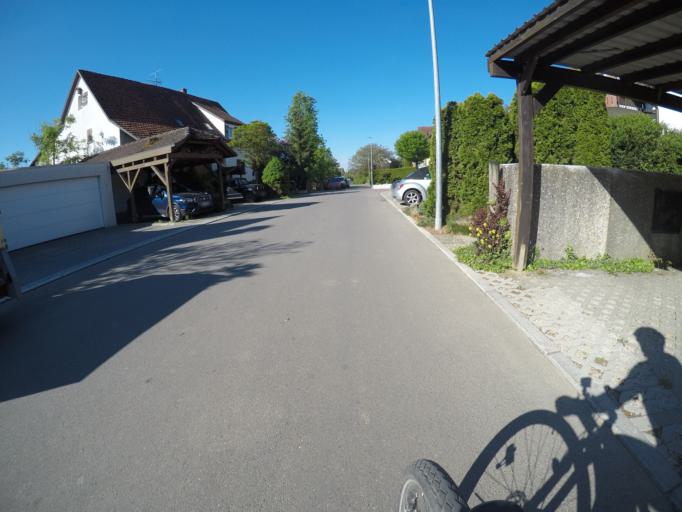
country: DE
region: Baden-Wuerttemberg
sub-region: Regierungsbezirk Stuttgart
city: Schlaitdorf
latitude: 48.6078
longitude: 9.2254
